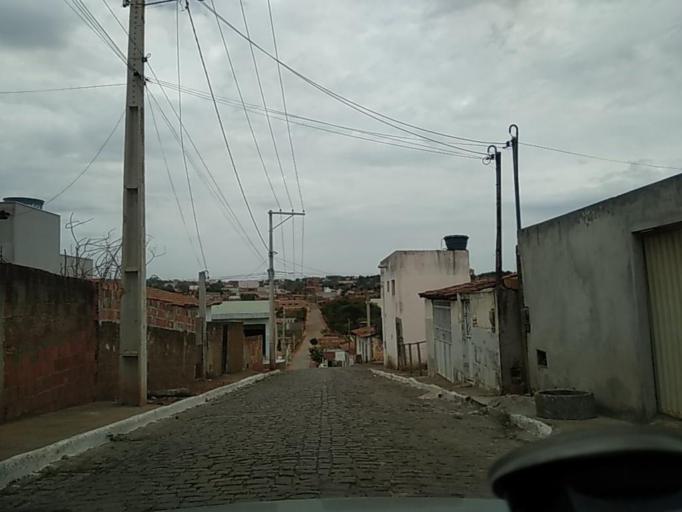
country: BR
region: Bahia
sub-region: Caetite
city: Caetite
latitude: -14.0543
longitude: -42.4798
